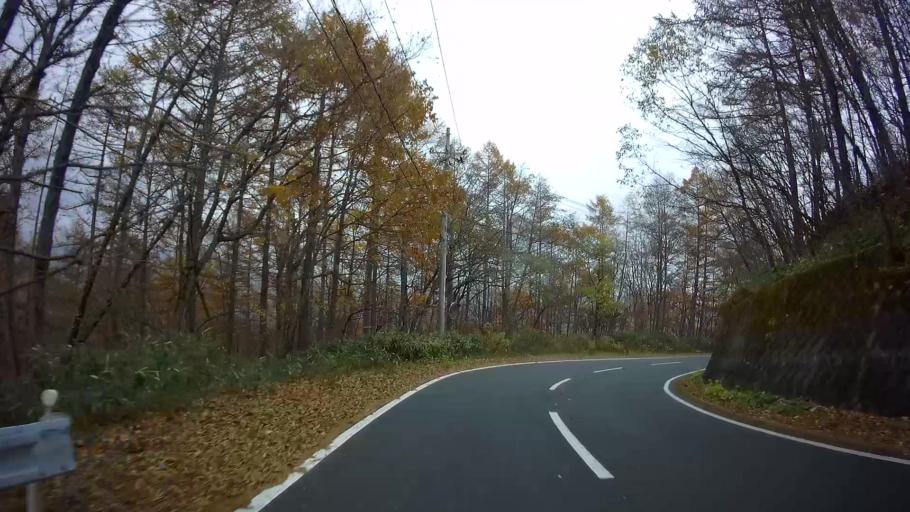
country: JP
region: Gunma
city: Nakanojomachi
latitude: 36.6732
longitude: 138.6663
